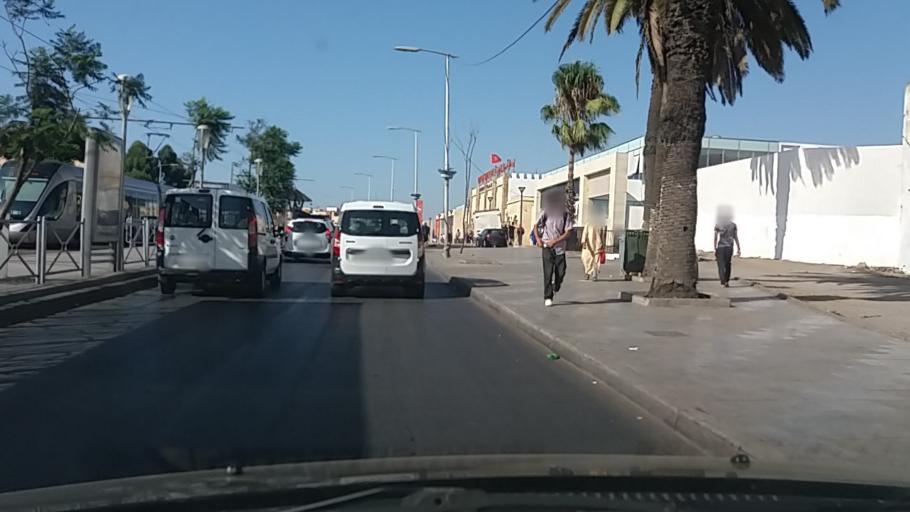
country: MA
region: Rabat-Sale-Zemmour-Zaer
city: Sale
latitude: 34.0377
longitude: -6.8163
